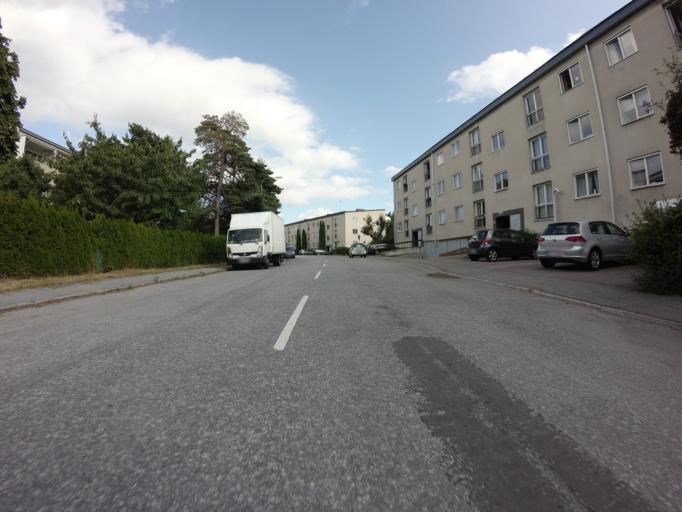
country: SE
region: Stockholm
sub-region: Lidingo
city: Lidingoe
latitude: 59.3748
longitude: 18.1400
